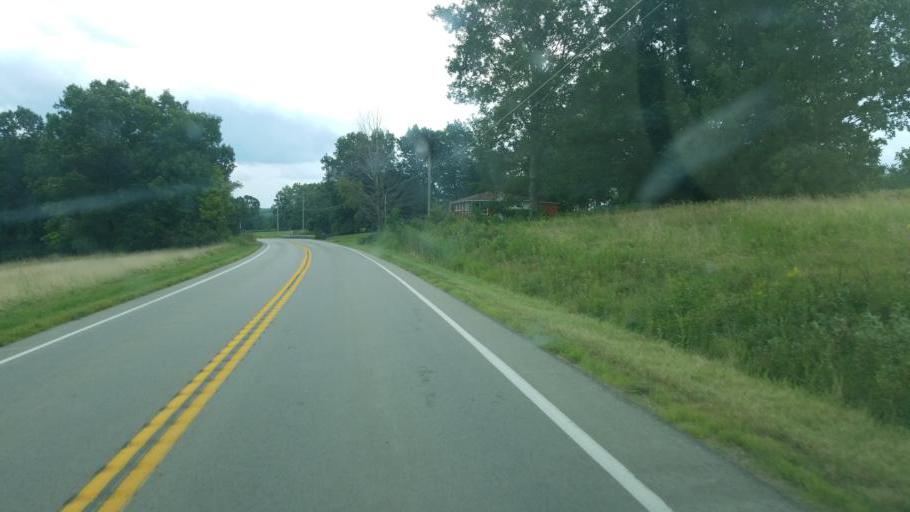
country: US
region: Pennsylvania
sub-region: Crawford County
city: Meadville
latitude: 41.5478
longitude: -80.2011
